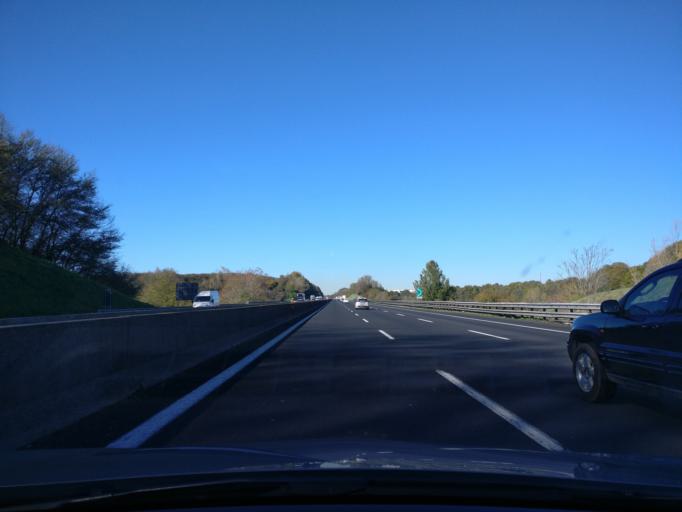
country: IT
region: Latium
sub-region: Citta metropolitana di Roma Capitale
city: Colleferro
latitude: 41.7532
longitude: 12.9787
